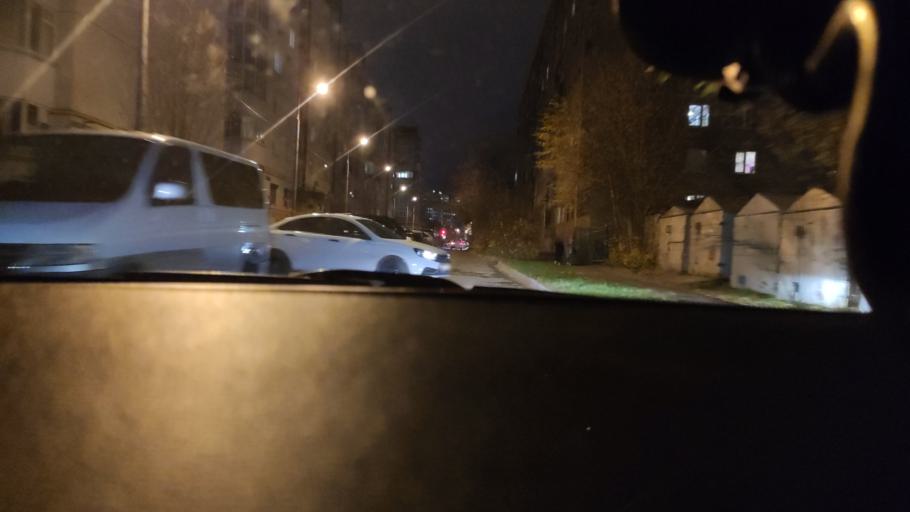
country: RU
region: Perm
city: Perm
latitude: 57.9973
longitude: 56.2293
